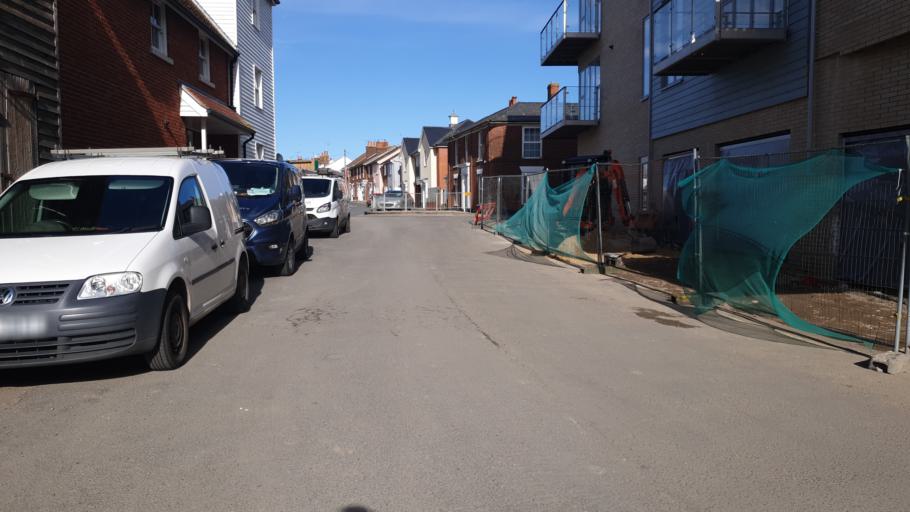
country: GB
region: England
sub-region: Essex
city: Brightlingsea
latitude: 51.8066
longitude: 1.0224
